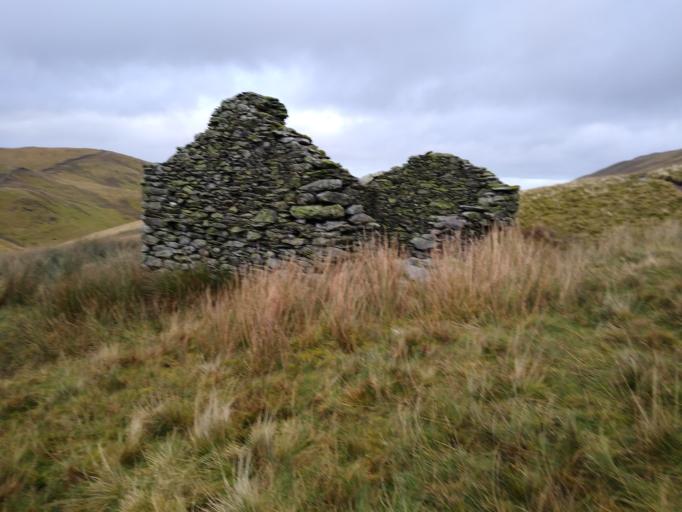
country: GB
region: England
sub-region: Cumbria
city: Ambleside
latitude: 54.5445
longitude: -2.8562
